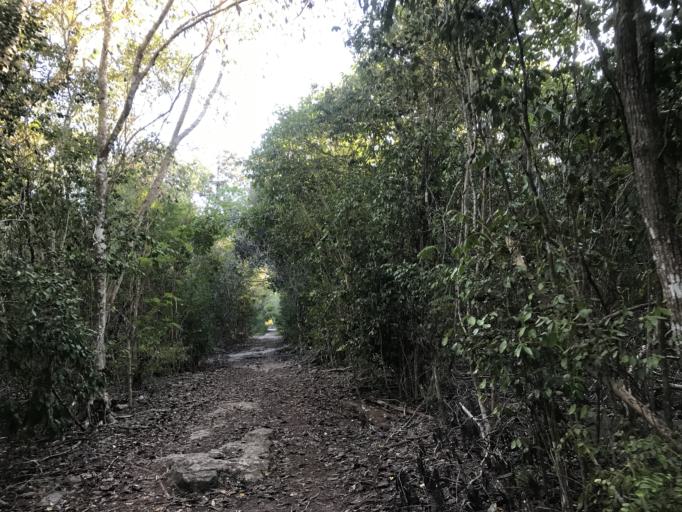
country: CU
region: Cienfuegos
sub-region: Municipio de Aguada de Pasajeros
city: Aguada de Pasajeros
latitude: 22.0815
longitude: -81.0720
